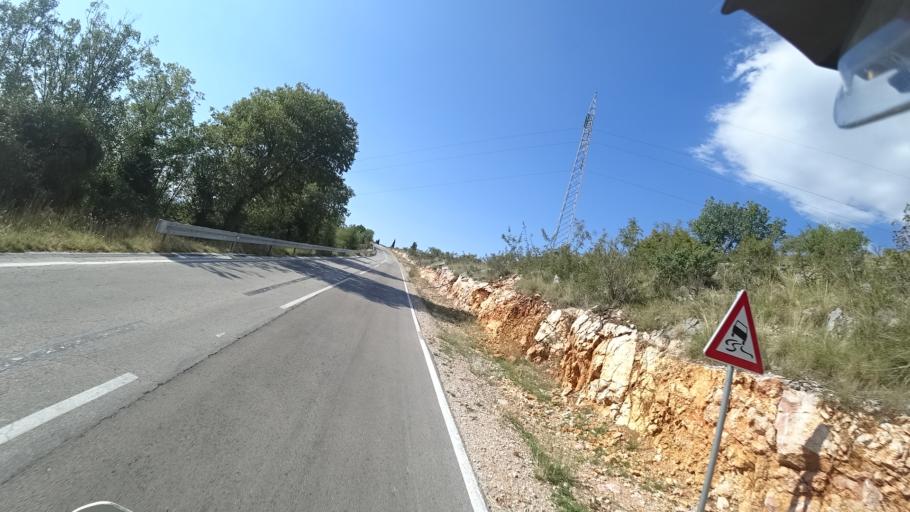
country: HR
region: Sibensko-Kniniska
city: Knin
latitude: 44.0117
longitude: 16.1965
